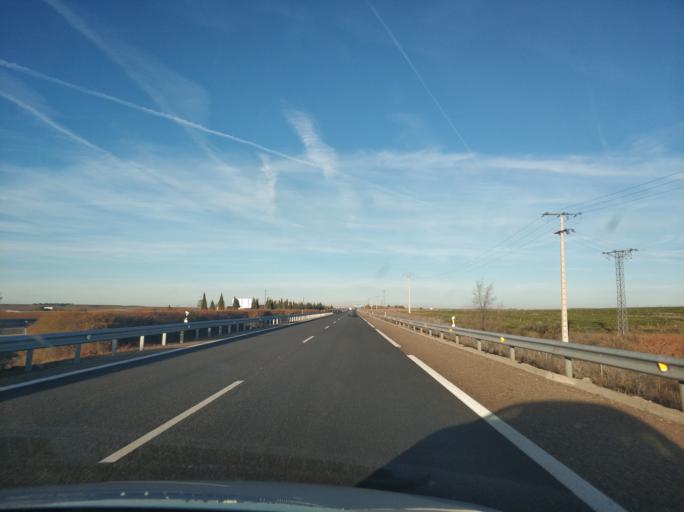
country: ES
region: Castille and Leon
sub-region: Provincia de Valladolid
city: Siete Iglesias de Trabancos
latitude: 41.3300
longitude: -5.1928
